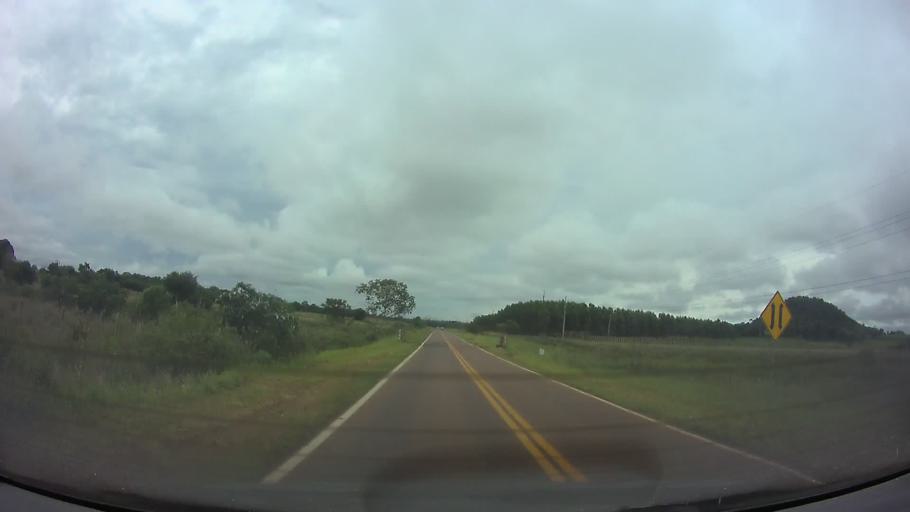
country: PY
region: Paraguari
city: Carapegua
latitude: -25.8091
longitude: -57.1820
